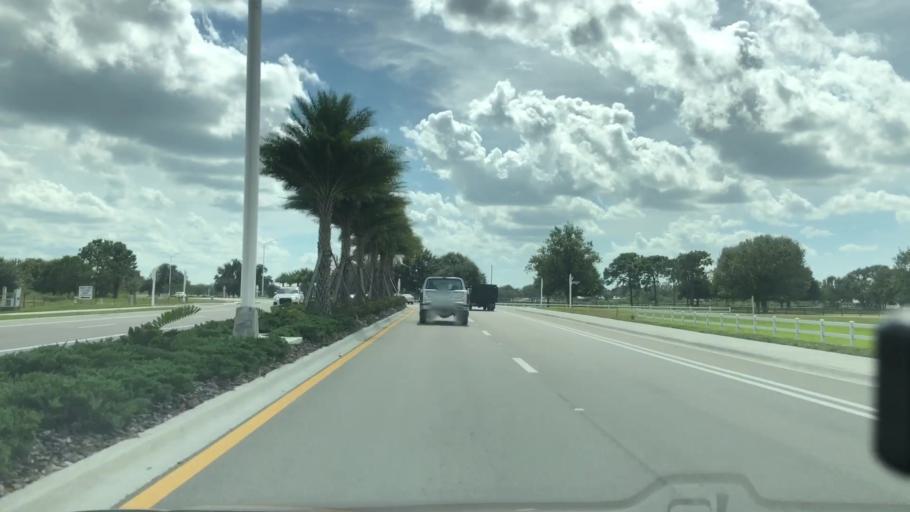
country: US
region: Florida
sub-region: Sarasota County
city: The Meadows
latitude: 27.3856
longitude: -82.3983
